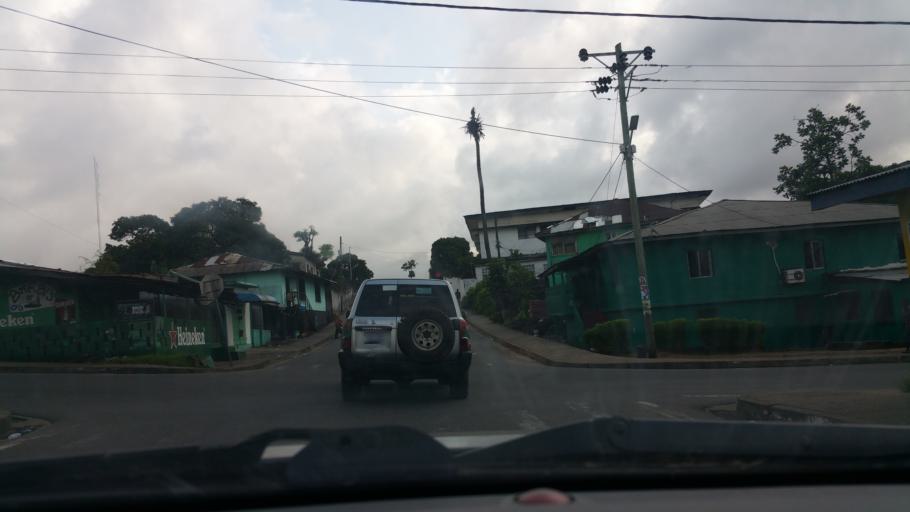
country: LR
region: Montserrado
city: Monrovia
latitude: 6.3173
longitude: -10.8102
